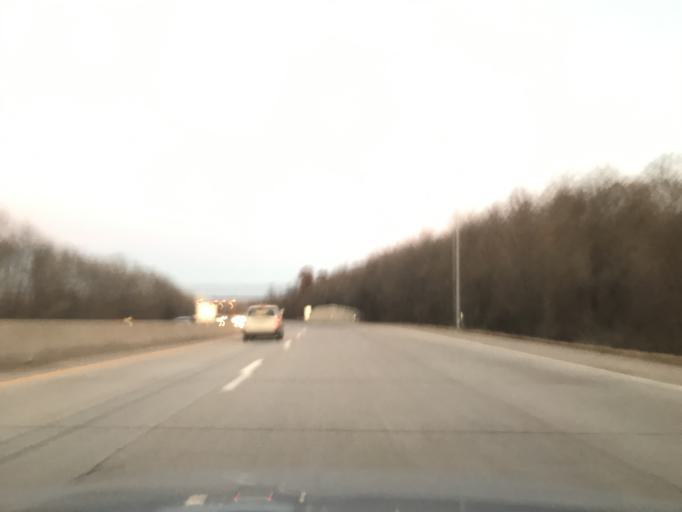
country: US
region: Missouri
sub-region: Marion County
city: Hannibal
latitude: 39.7181
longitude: -91.3663
